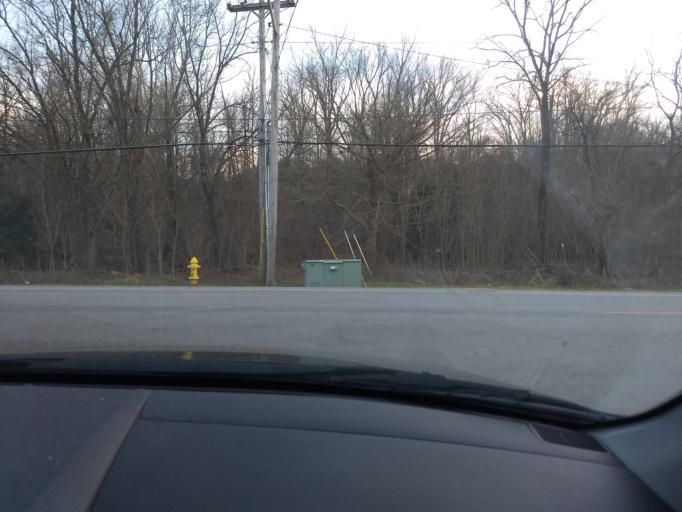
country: US
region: Indiana
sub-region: Floyd County
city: Georgetown
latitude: 38.2958
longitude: -85.9835
